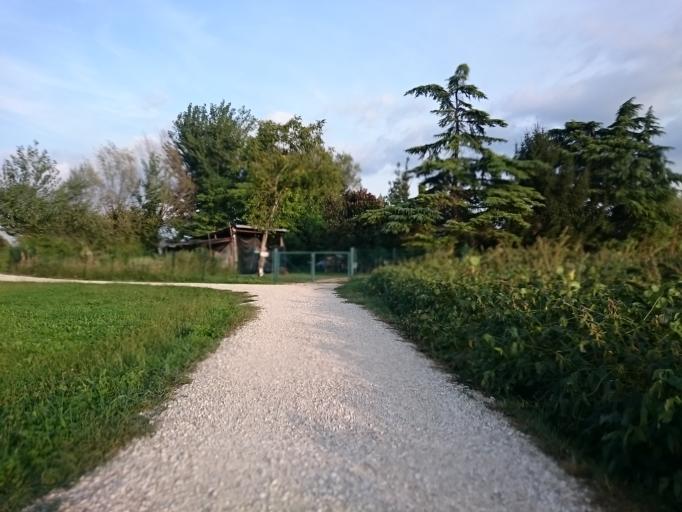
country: IT
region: Veneto
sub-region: Provincia di Vicenza
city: Camisano Vicentino
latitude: 45.5122
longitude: 11.7251
